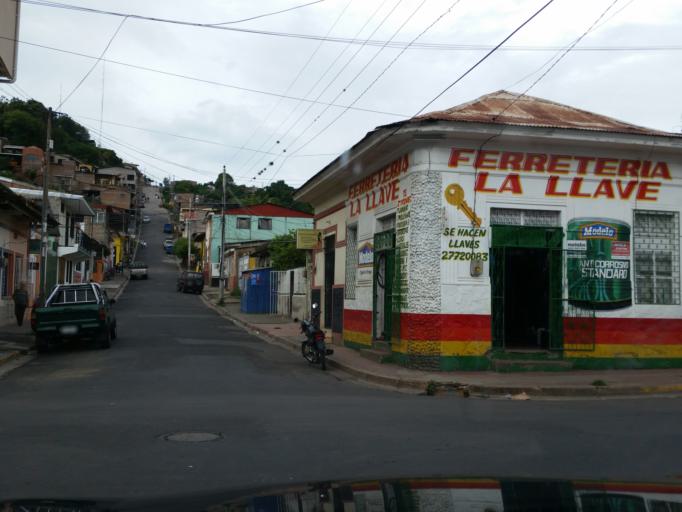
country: NI
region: Matagalpa
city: Matagalpa
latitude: 12.9296
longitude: -85.9155
